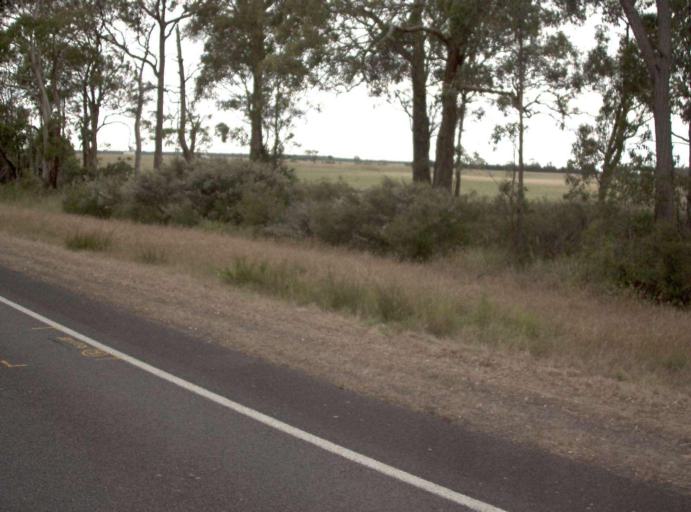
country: AU
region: Victoria
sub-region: Wellington
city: Sale
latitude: -38.4877
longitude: 146.9121
